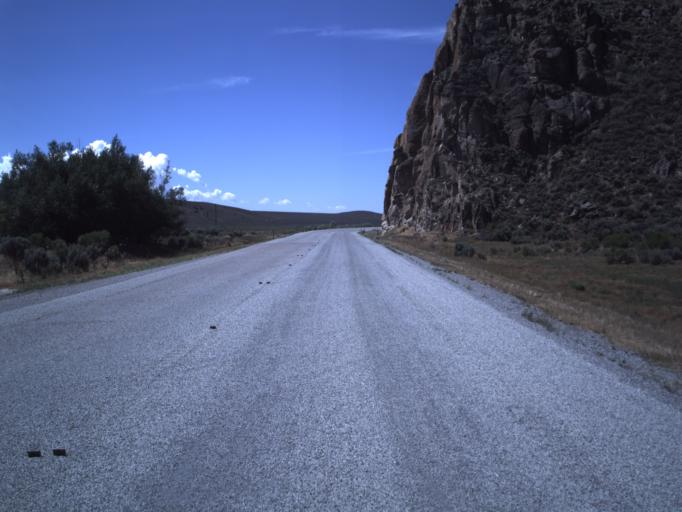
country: US
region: Utah
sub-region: Garfield County
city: Panguitch
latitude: 38.0286
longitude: -112.3578
